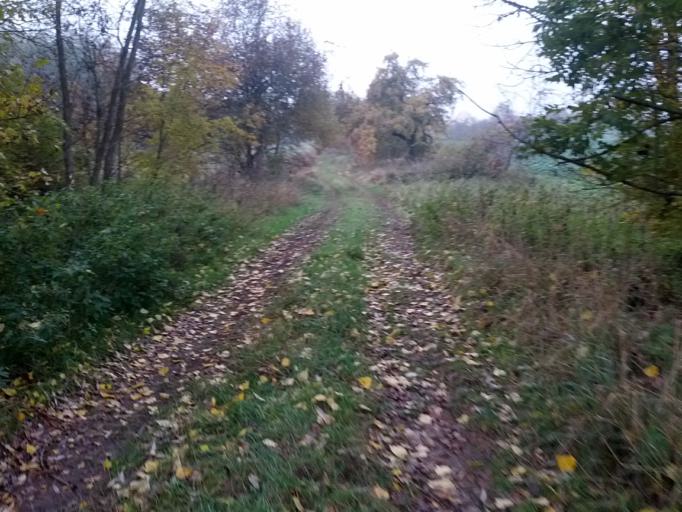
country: DE
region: Thuringia
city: Eisenach
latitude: 50.9934
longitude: 10.3678
